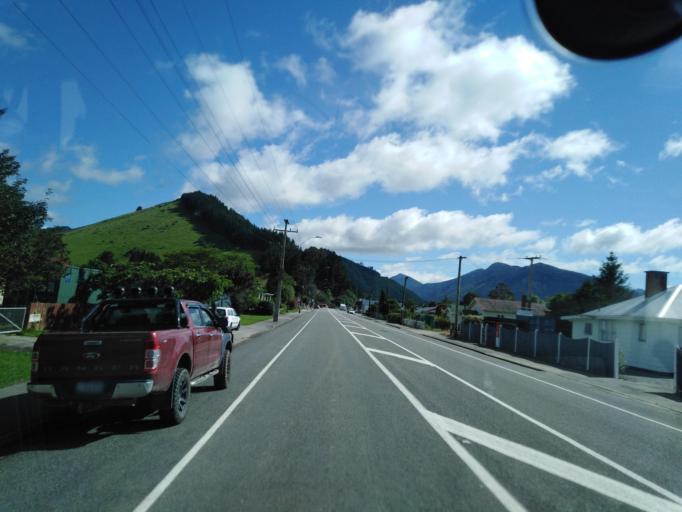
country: NZ
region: Nelson
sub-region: Nelson City
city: Nelson
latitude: -41.2299
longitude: 173.5823
